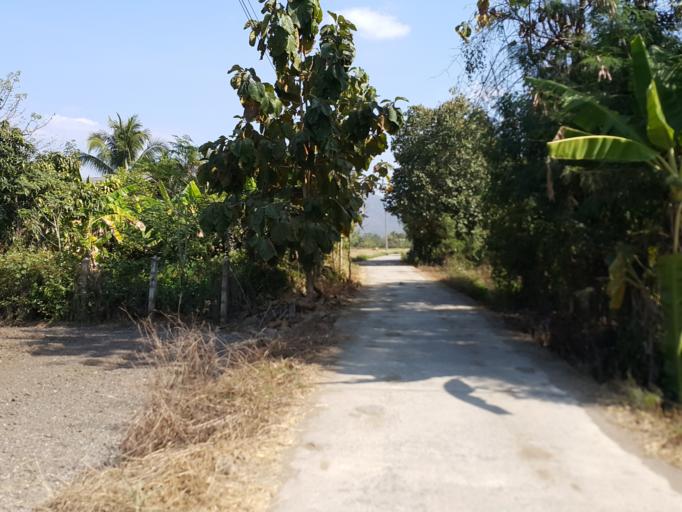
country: TH
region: Chiang Mai
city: San Kamphaeng
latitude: 18.8078
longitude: 99.1605
